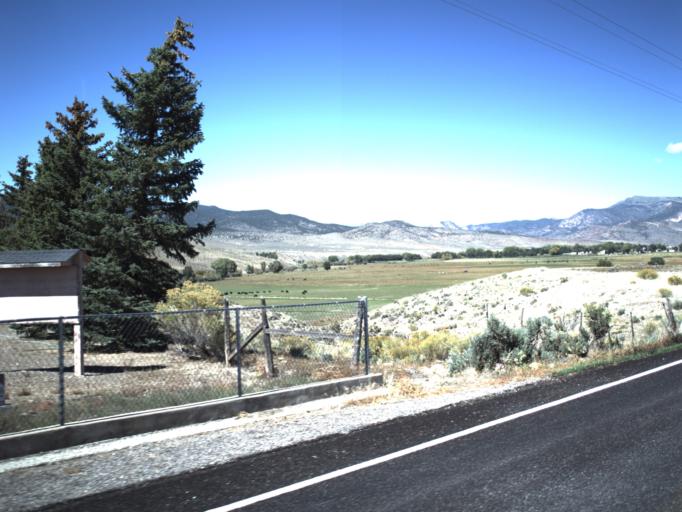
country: US
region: Utah
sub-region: Piute County
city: Junction
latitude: 38.0960
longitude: -111.9836
